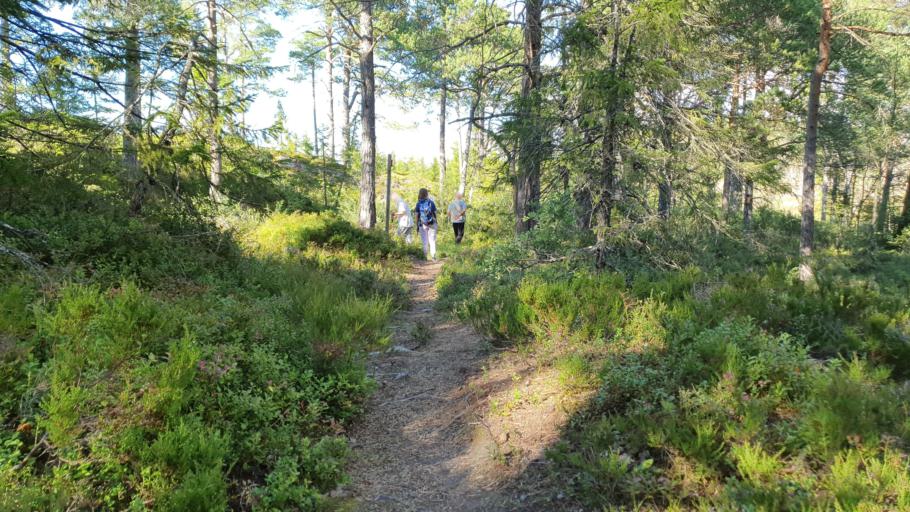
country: NO
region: Nord-Trondelag
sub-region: Levanger
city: Levanger
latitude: 63.6921
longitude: 11.2720
